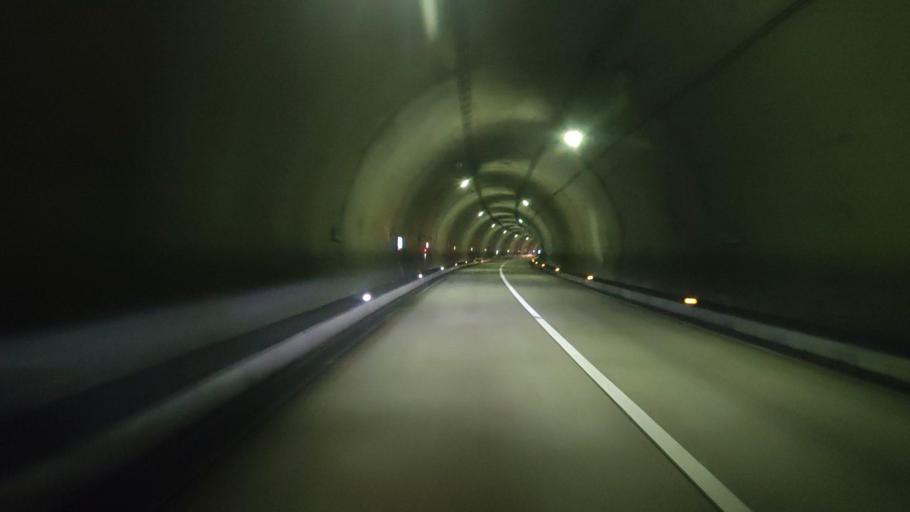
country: JP
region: Wakayama
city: Shingu
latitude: 33.8520
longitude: 135.8557
